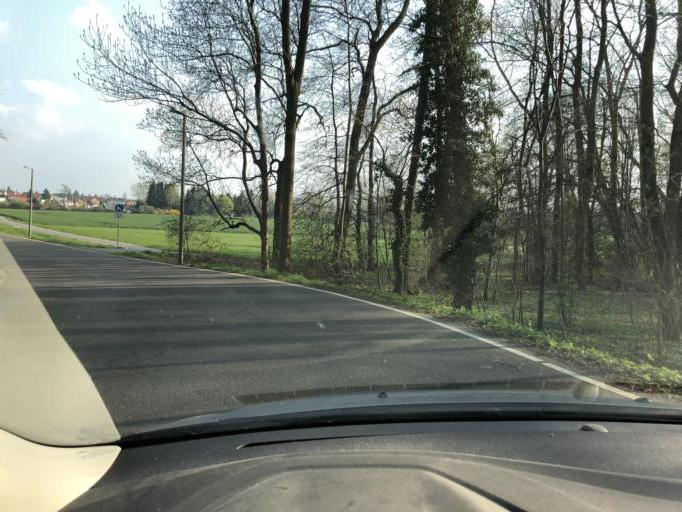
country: DE
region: Saxony
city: Taucha
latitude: 51.3910
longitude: 12.4559
